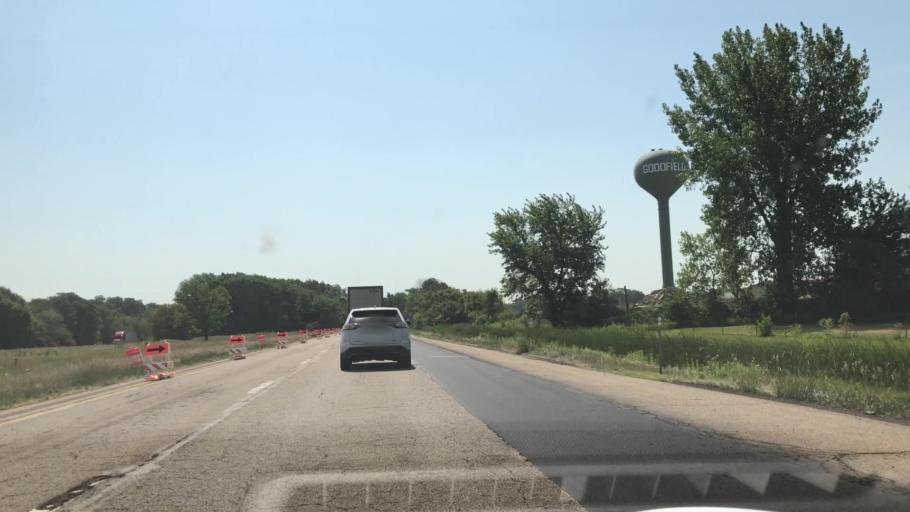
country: US
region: Illinois
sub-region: Woodford County
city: Eureka
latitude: 40.6204
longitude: -89.2685
